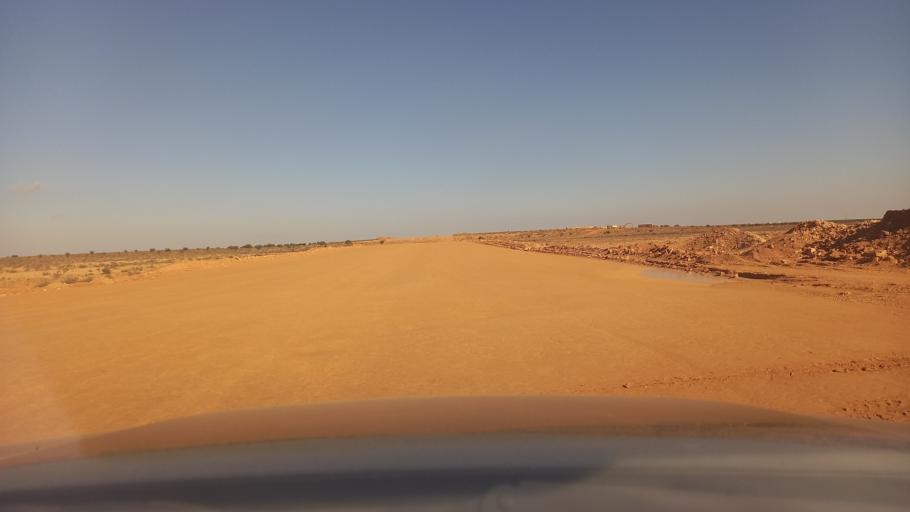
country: TN
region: Madanin
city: Medenine
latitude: 33.1705
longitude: 10.5261
